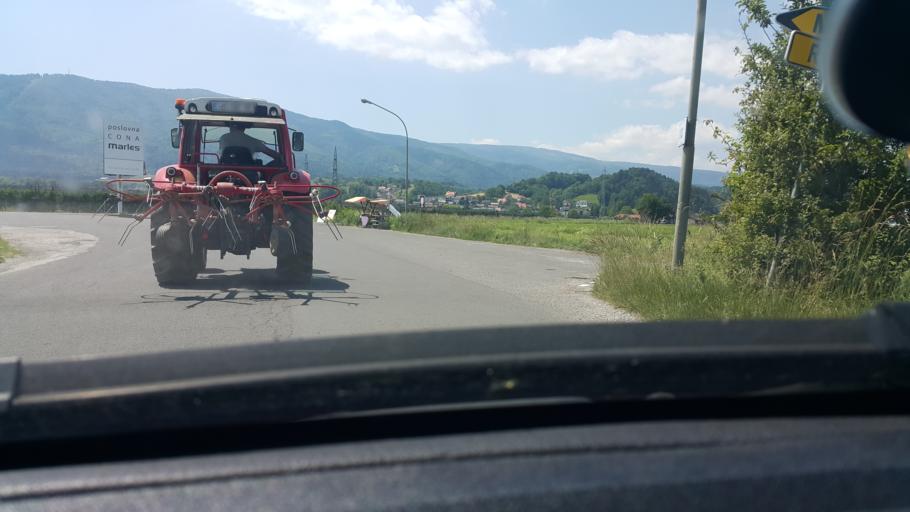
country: SI
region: Maribor
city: Pekre
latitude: 46.5583
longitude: 15.5968
